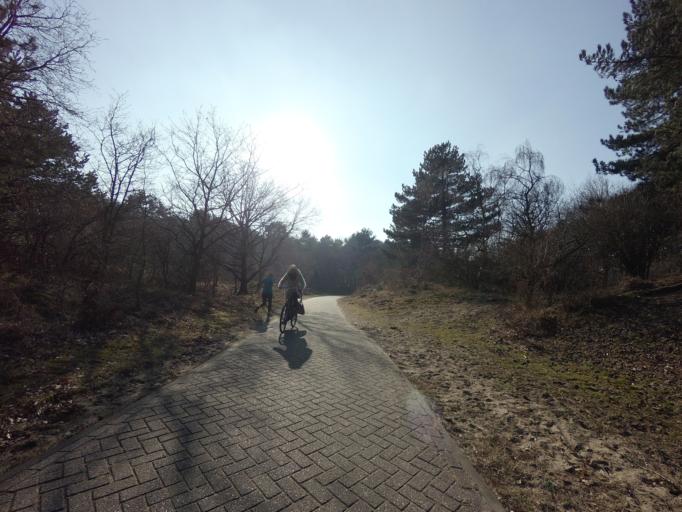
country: NL
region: North Holland
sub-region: Gemeente Bloemendaal
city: Bloemendaal
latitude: 52.4108
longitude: 4.6034
